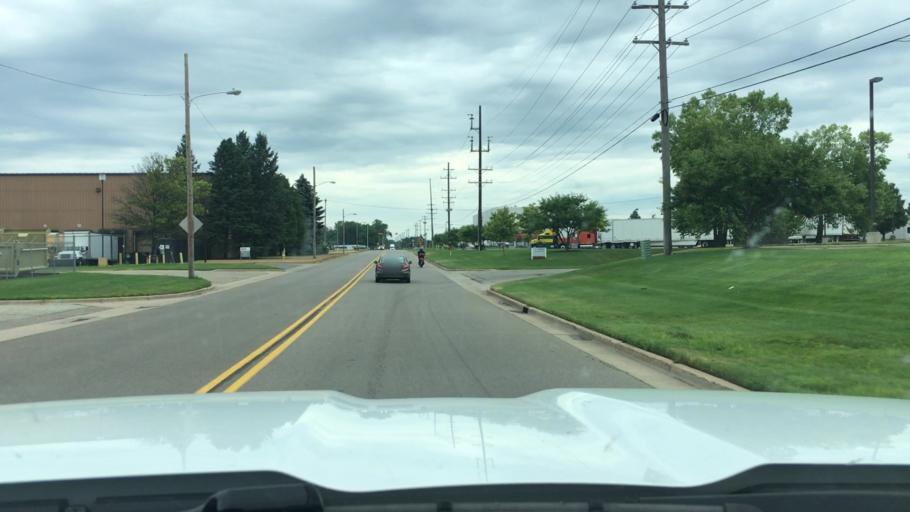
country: US
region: Michigan
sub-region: Kent County
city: Kentwood
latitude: 42.8708
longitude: -85.6776
